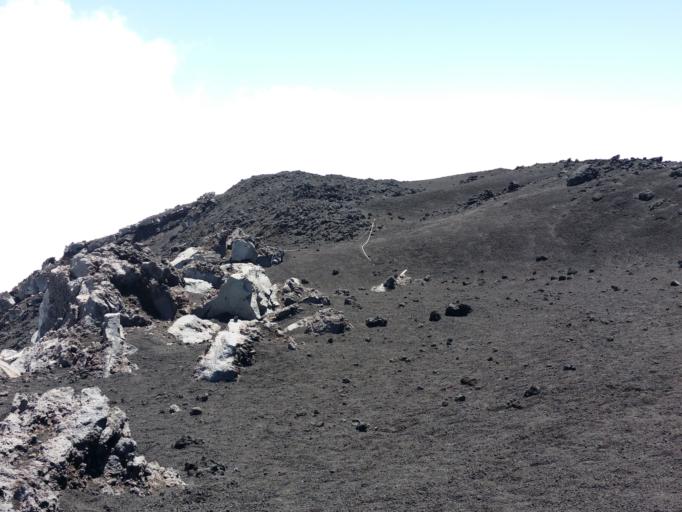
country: IT
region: Sicily
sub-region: Catania
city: Milo
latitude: 37.7334
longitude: 15.0098
